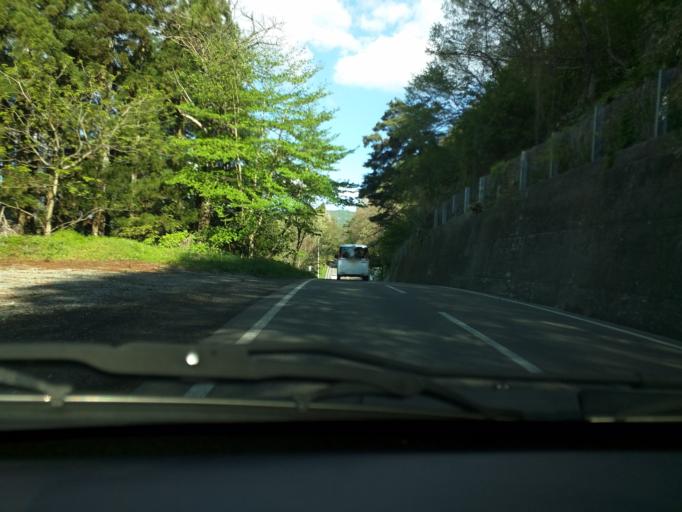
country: JP
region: Nagano
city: Nagano-shi
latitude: 36.6827
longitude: 138.1651
